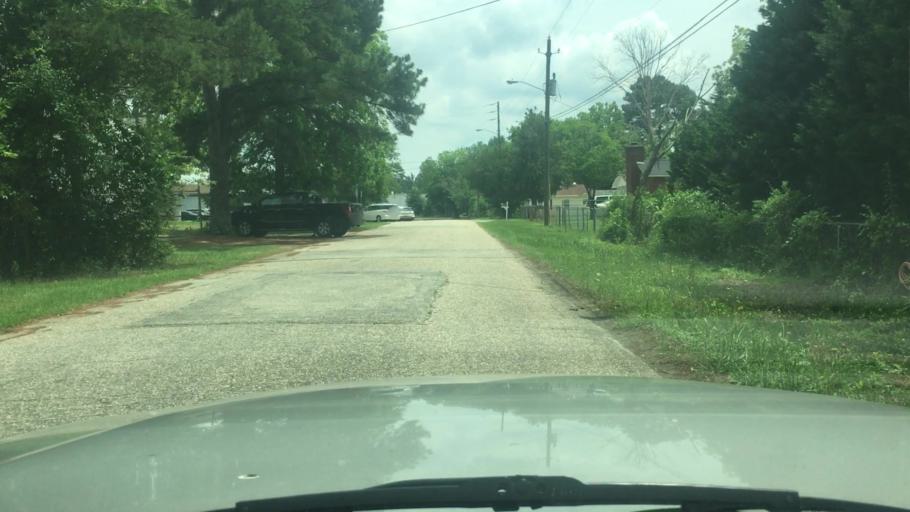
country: US
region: North Carolina
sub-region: Cumberland County
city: Fort Bragg
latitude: 35.0923
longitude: -78.9563
